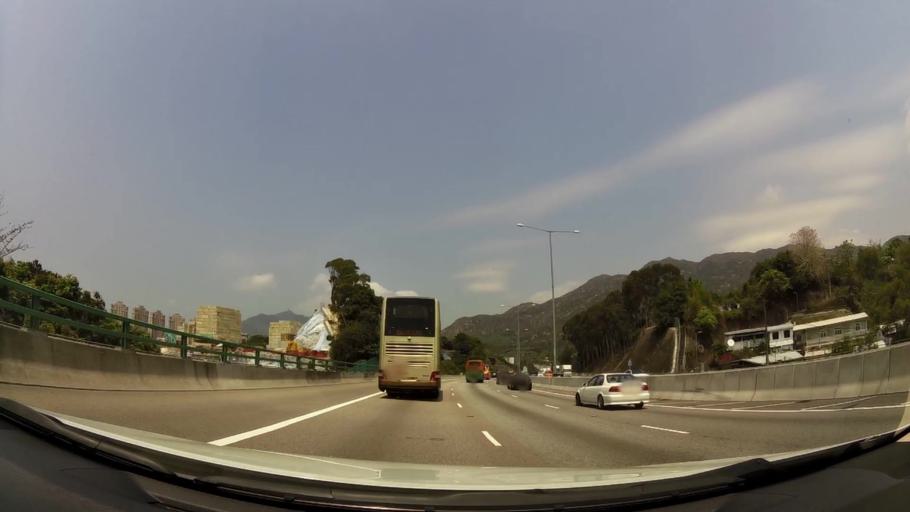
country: HK
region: Tuen Mun
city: Tuen Mun
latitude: 22.3681
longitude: 114.0013
